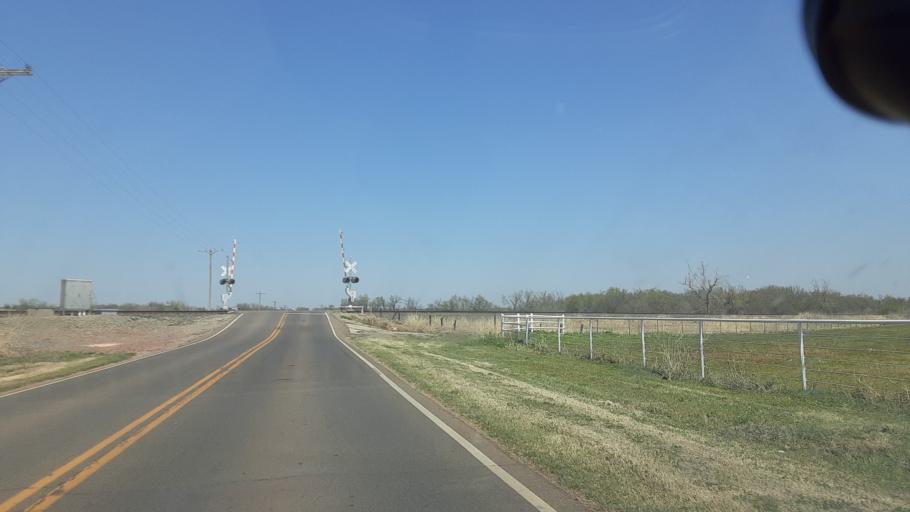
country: US
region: Oklahoma
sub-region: Logan County
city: Guthrie
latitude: 35.8071
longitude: -97.4784
